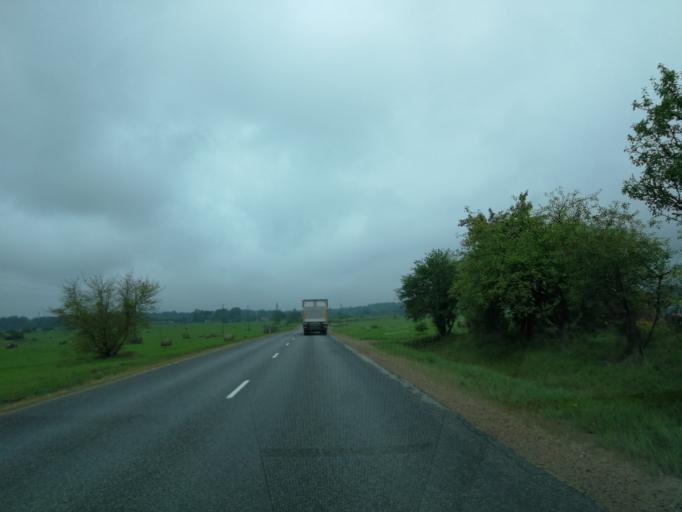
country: LV
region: Livani
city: Livani
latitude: 56.3545
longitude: 26.2399
